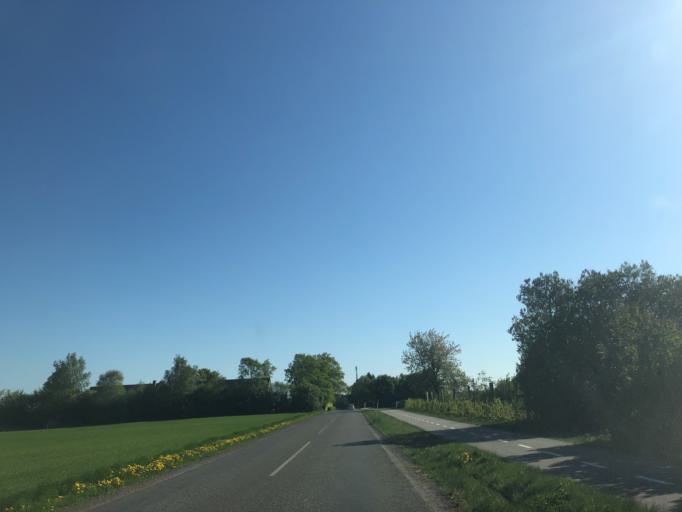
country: DK
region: Zealand
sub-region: Ringsted Kommune
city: Ringsted
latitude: 55.4430
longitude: 11.7279
